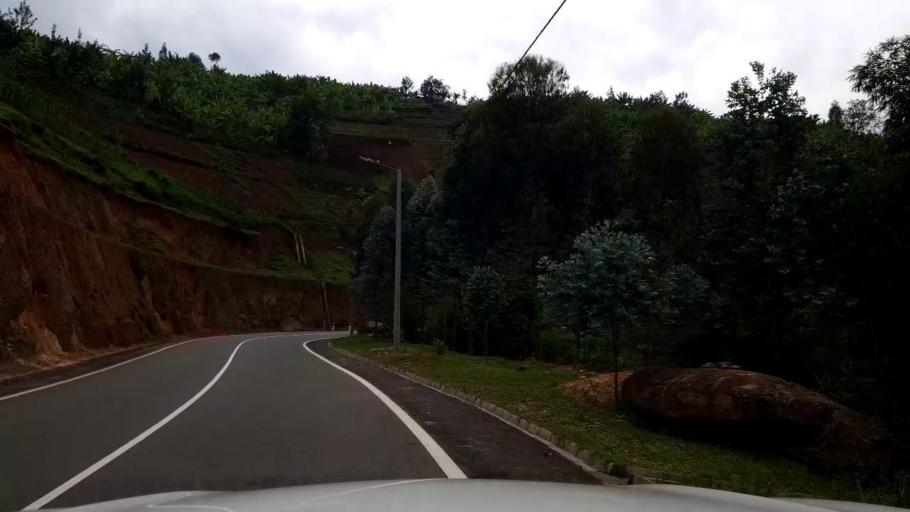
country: RW
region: Western Province
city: Kibuye
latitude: -1.9280
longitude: 29.3730
